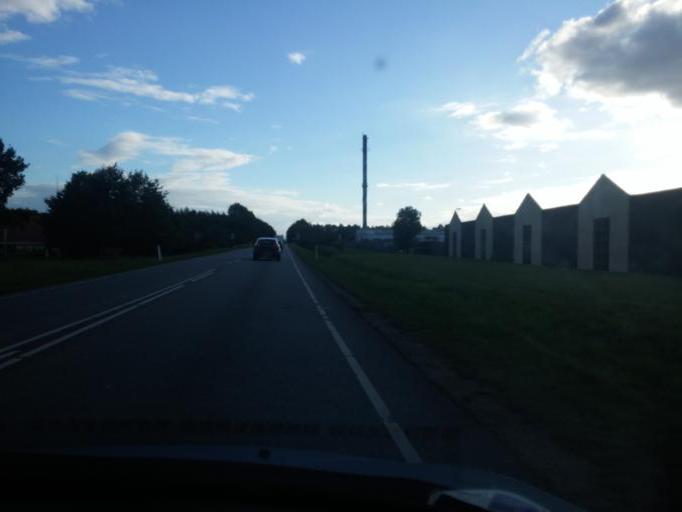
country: DK
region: South Denmark
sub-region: Odense Kommune
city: Bellinge
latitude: 55.3568
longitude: 10.3395
